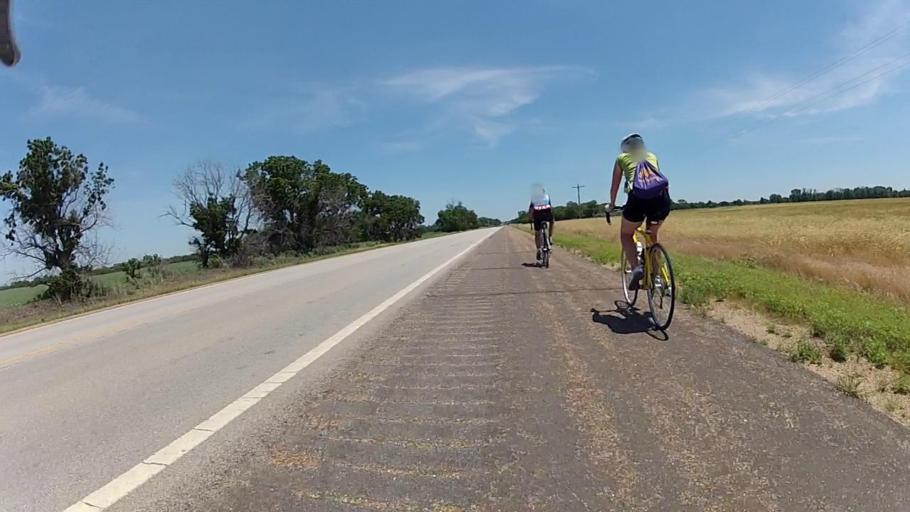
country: US
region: Kansas
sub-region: Barber County
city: Medicine Lodge
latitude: 37.2534
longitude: -98.3386
